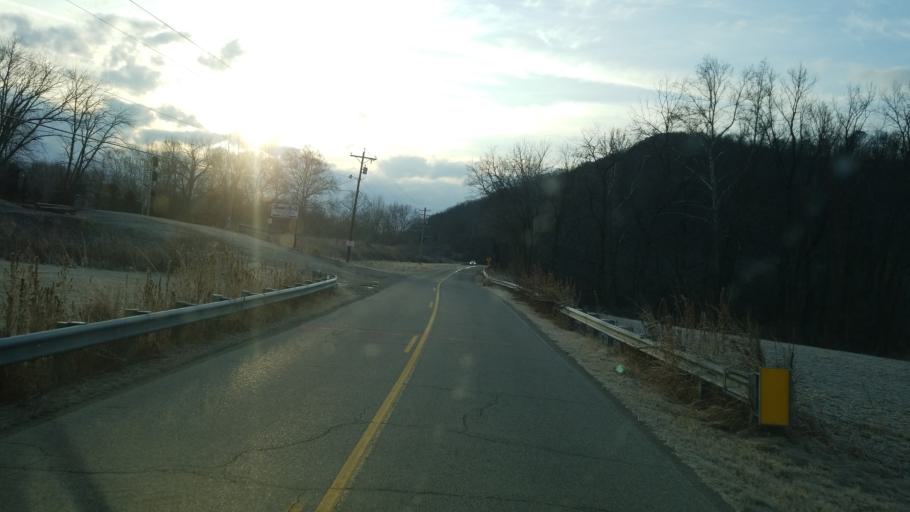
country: US
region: Ohio
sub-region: Ross County
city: Chillicothe
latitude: 39.2858
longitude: -82.9397
